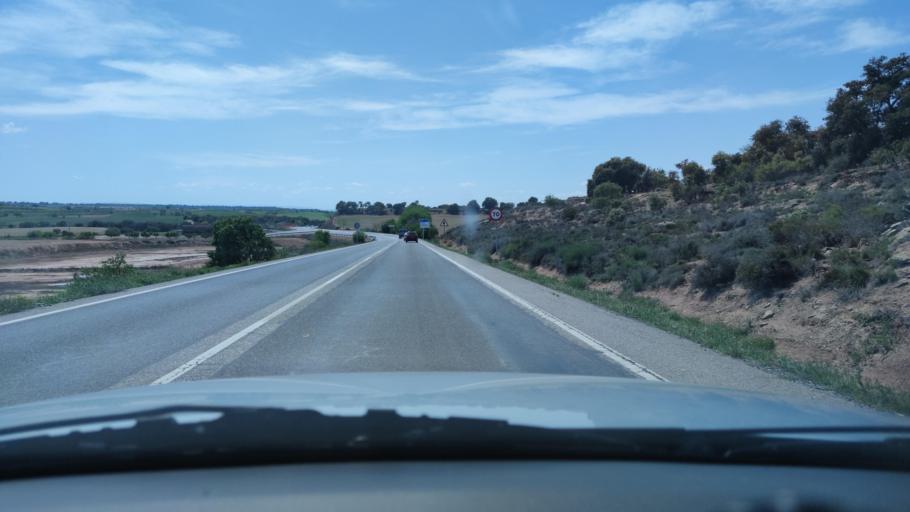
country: ES
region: Catalonia
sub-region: Provincia de Lleida
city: Mont-roig del Camp
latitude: 41.7160
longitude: 1.1940
